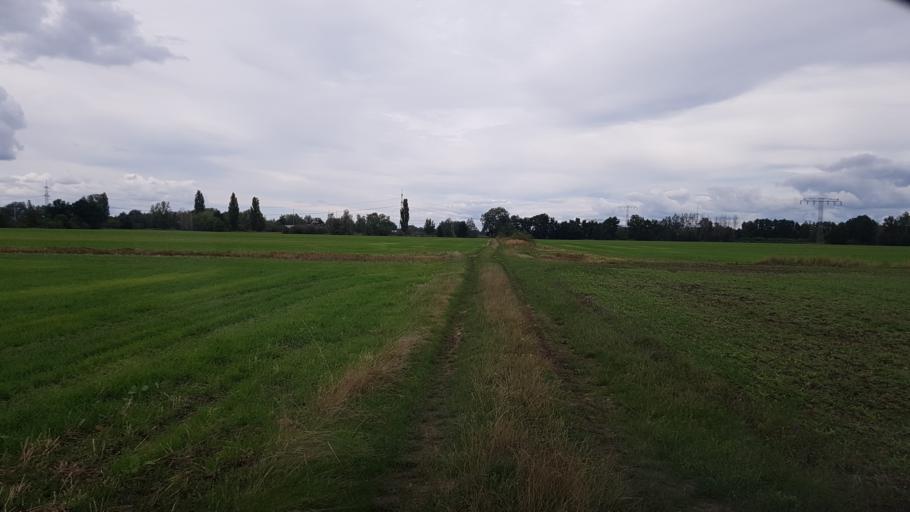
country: DE
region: Brandenburg
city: Doberlug-Kirchhain
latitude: 51.6401
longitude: 13.5836
